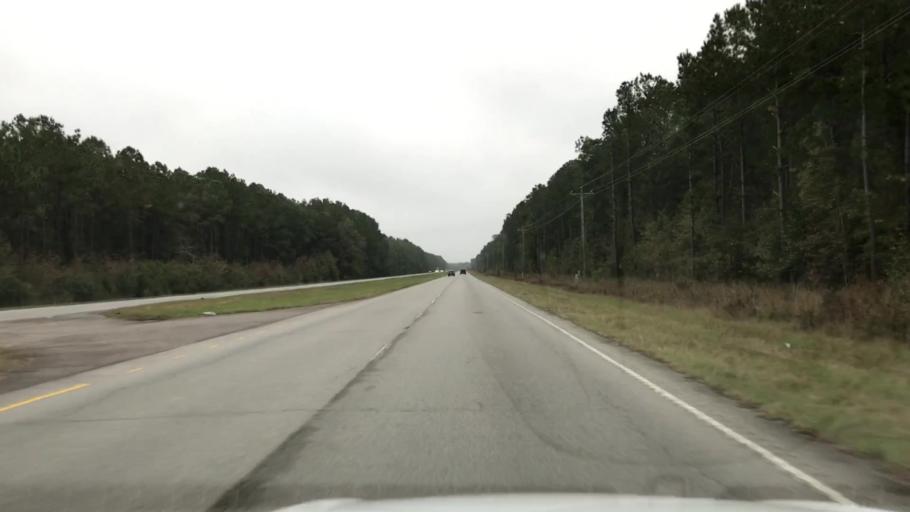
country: US
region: South Carolina
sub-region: Charleston County
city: Awendaw
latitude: 33.0118
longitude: -79.6375
